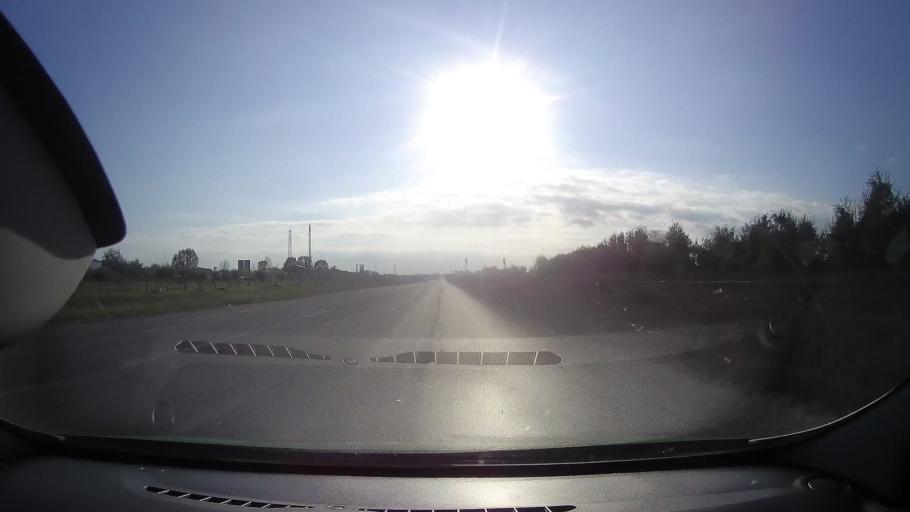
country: RO
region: Constanta
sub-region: Comuna Navodari
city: Navodari
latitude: 44.3376
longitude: 28.6358
